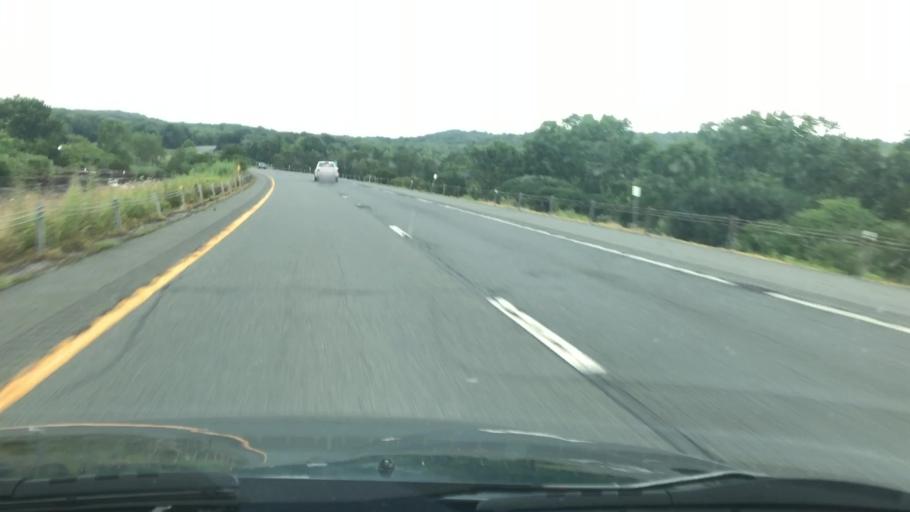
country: US
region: New York
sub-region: Orange County
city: Otisville
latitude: 41.3837
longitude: -74.5765
